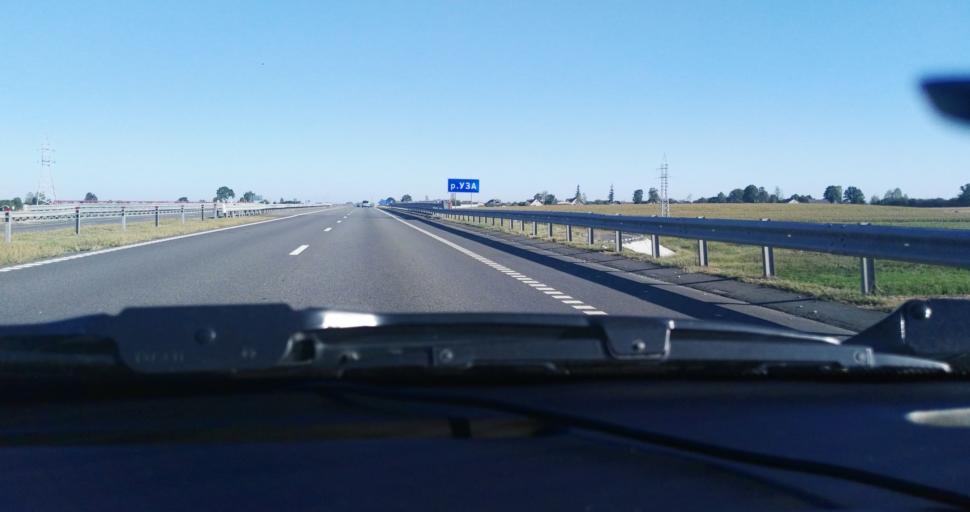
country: BY
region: Gomel
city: Buda-Kashalyova
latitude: 52.5135
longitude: 30.6297
